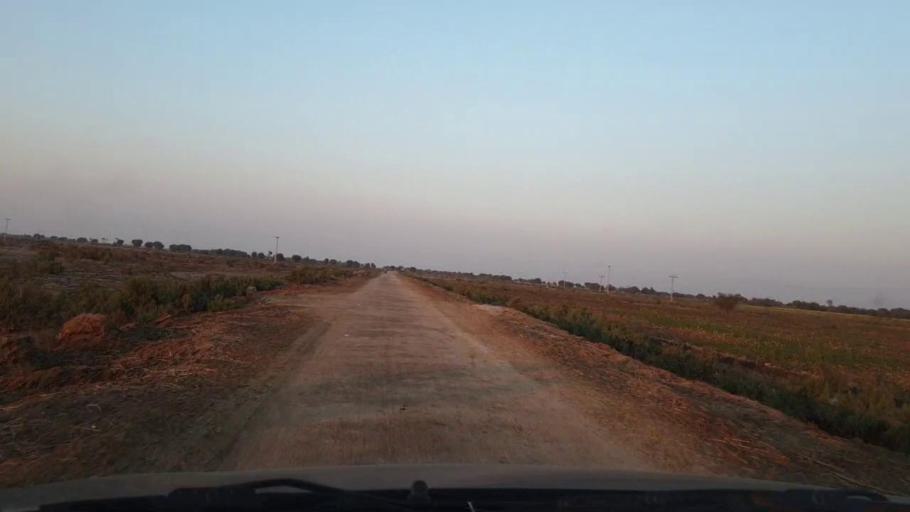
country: PK
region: Sindh
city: Jhol
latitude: 25.9288
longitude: 68.9667
